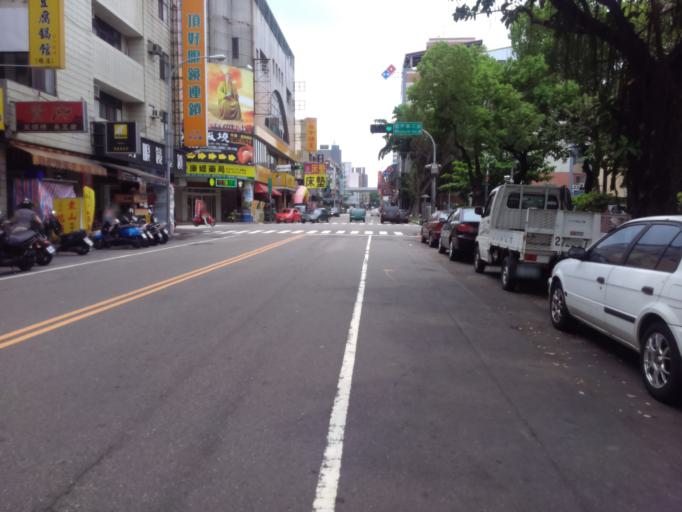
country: TW
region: Taiwan
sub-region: Taichung City
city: Taichung
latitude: 24.1710
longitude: 120.6759
